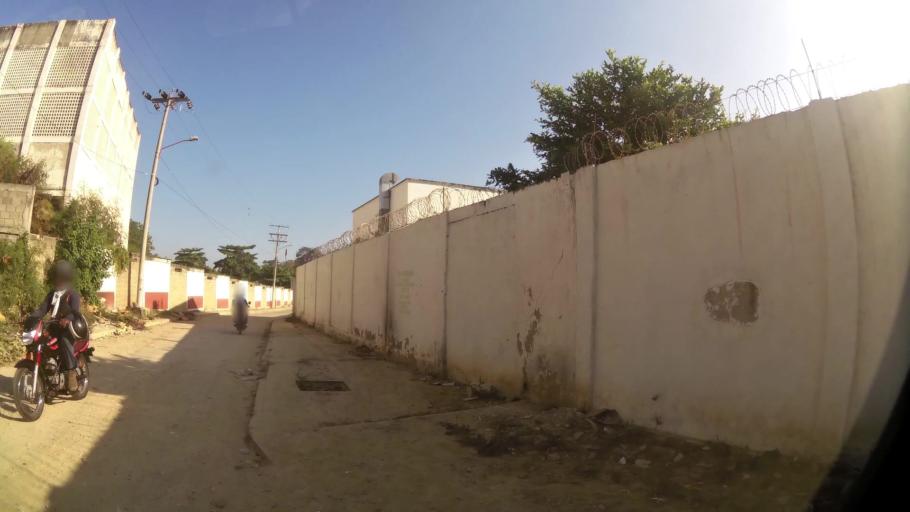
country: CO
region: Bolivar
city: Cartagena
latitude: 10.4009
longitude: -75.5048
